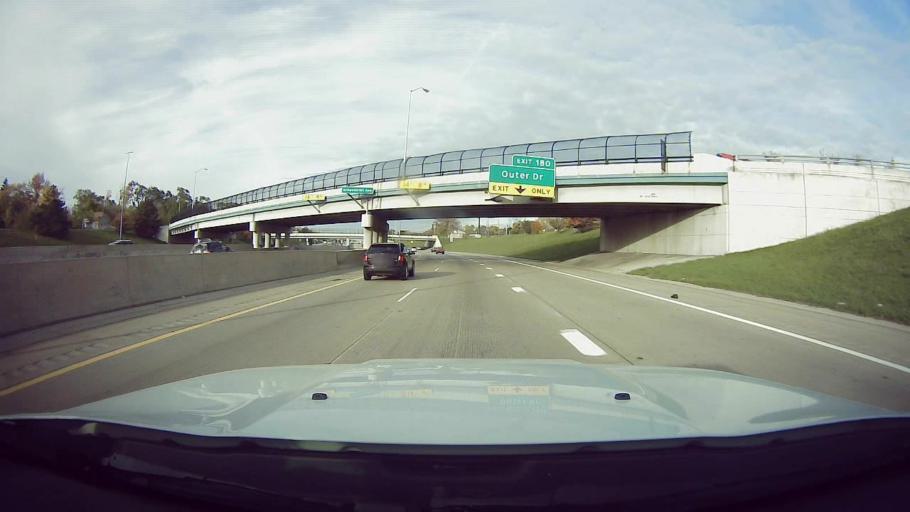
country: US
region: Michigan
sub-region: Wayne County
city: Redford
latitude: 42.3856
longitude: -83.2441
